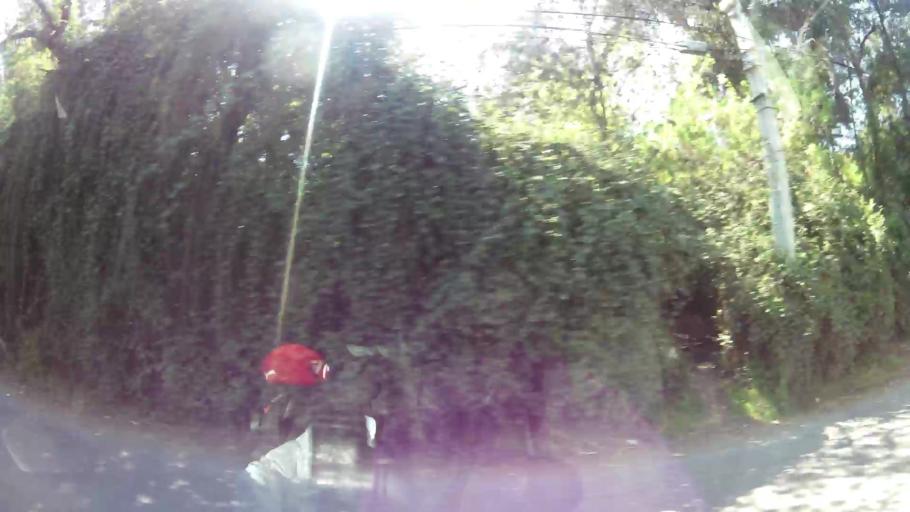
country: CL
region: Santiago Metropolitan
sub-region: Provincia de Santiago
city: Villa Presidente Frei, Nunoa, Santiago, Chile
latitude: -33.4342
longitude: -70.5185
